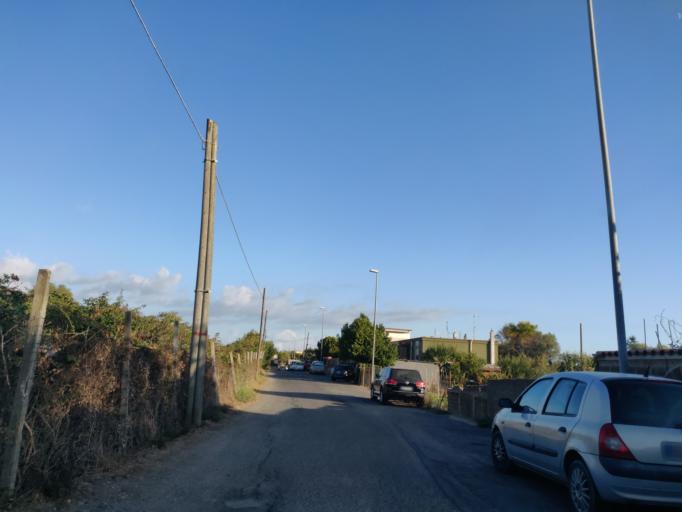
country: IT
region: Latium
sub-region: Citta metropolitana di Roma Capitale
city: Civitavecchia
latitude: 42.0922
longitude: 11.8134
